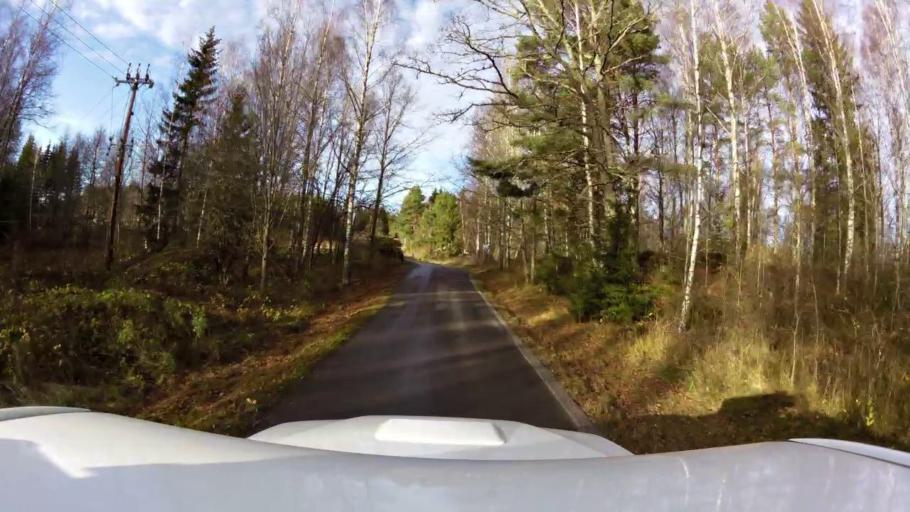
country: SE
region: OEstergoetland
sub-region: Linkopings Kommun
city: Sturefors
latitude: 58.2602
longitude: 15.6914
